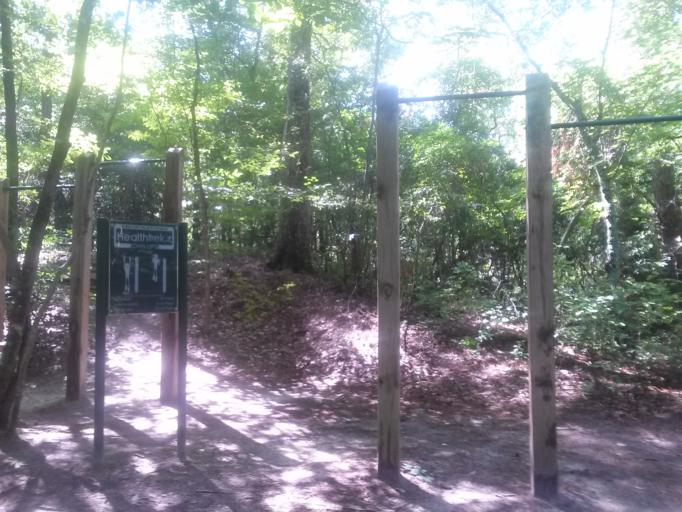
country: US
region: Virginia
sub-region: City of Virginia Beach
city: Virginia Beach
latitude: 36.9093
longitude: -76.0238
